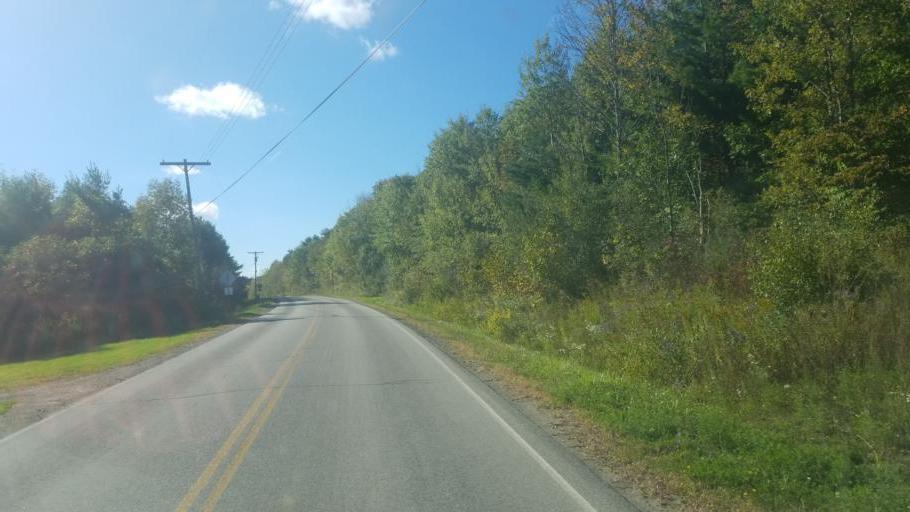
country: US
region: New York
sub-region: Allegany County
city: Friendship
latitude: 42.2764
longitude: -78.1560
